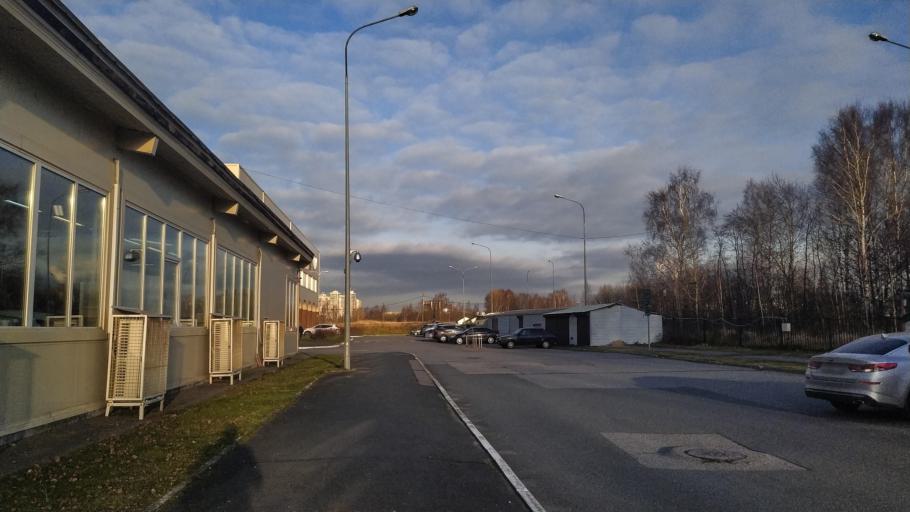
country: RU
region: Leningrad
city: Murino
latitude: 60.0183
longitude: 30.4361
